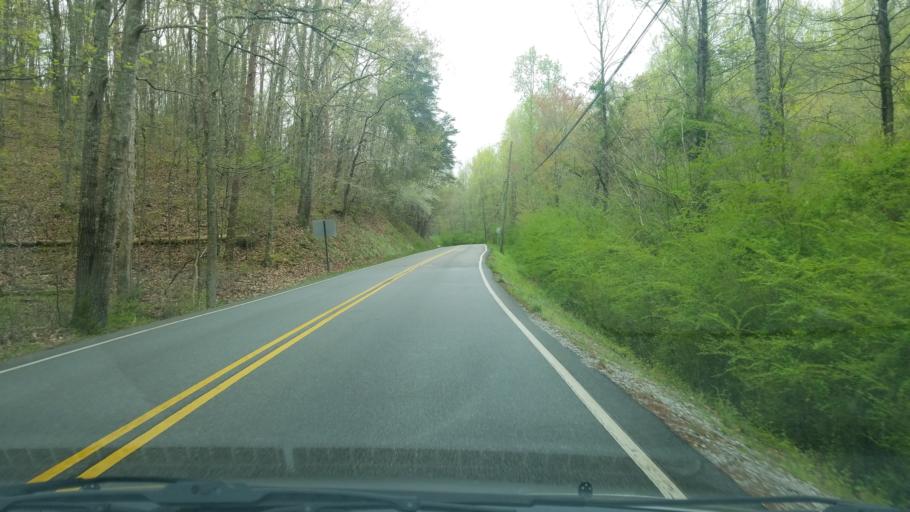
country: US
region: Tennessee
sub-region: Hamilton County
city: Collegedale
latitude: 35.0212
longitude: -85.0709
